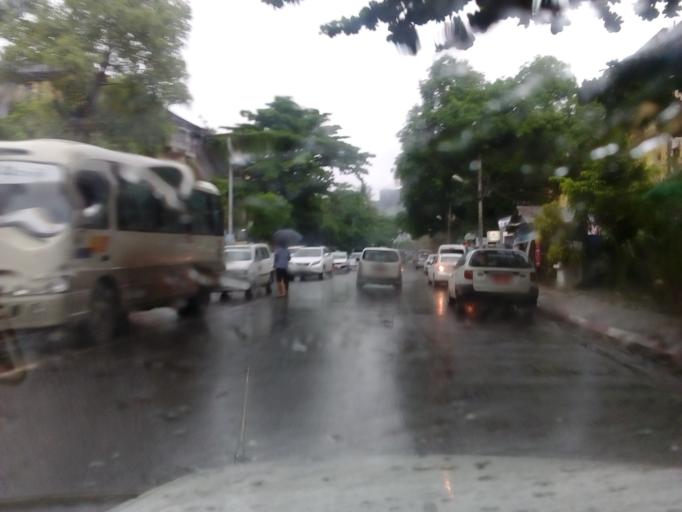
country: MM
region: Yangon
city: Yangon
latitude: 16.8303
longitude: 96.1634
